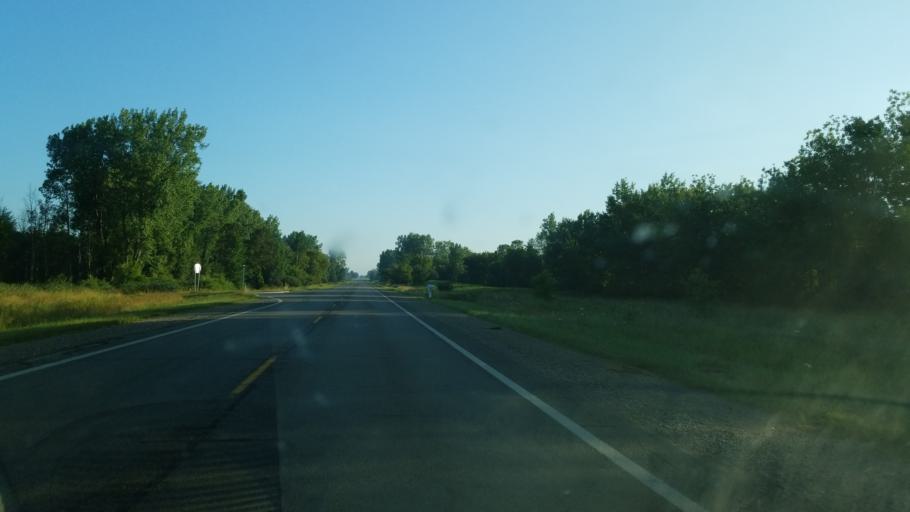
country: US
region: Michigan
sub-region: Montcalm County
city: Edmore
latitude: 43.3643
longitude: -85.0850
